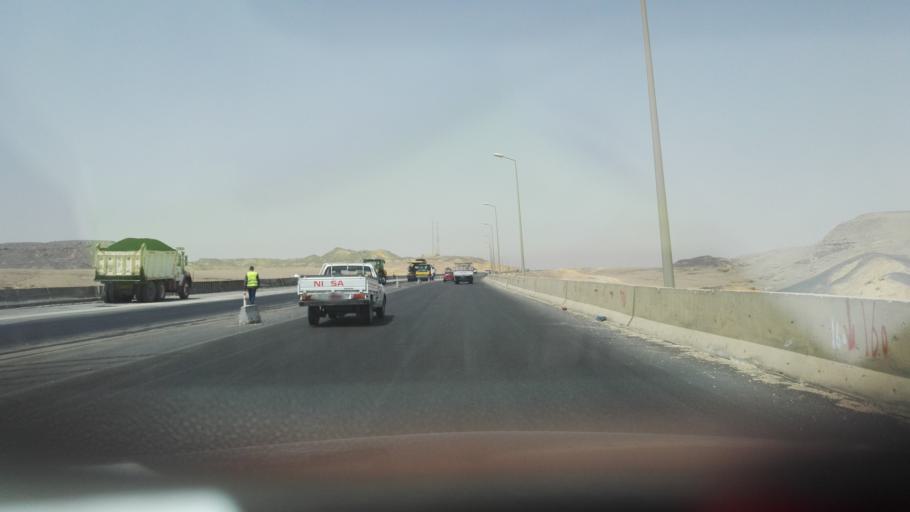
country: EG
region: As Suways
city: Ain Sukhna
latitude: 29.6958
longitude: 32.1113
